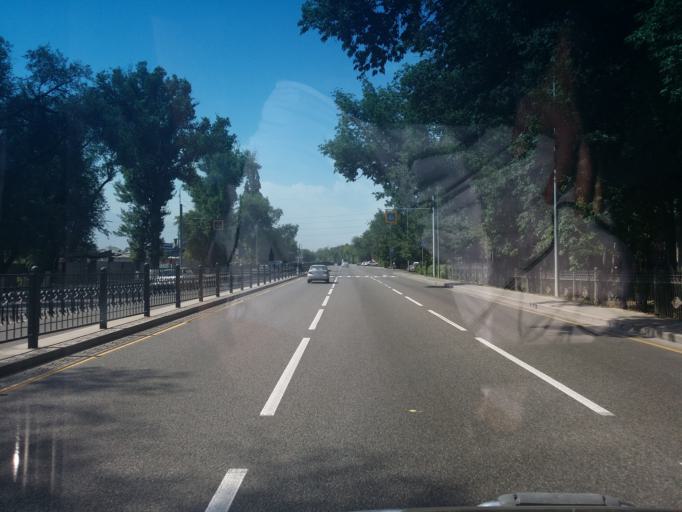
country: KZ
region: Almaty Qalasy
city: Almaty
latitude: 43.2936
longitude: 76.9949
